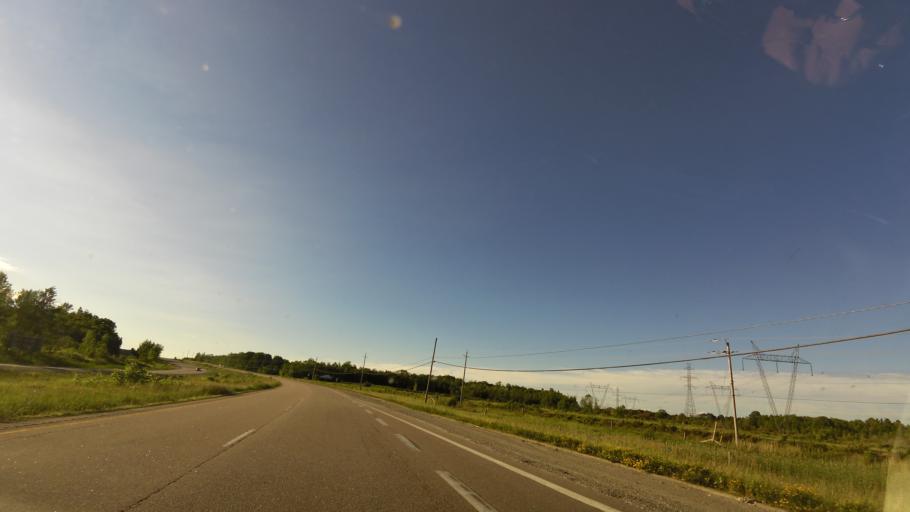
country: CA
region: Ontario
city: Midland
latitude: 44.7740
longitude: -79.6907
